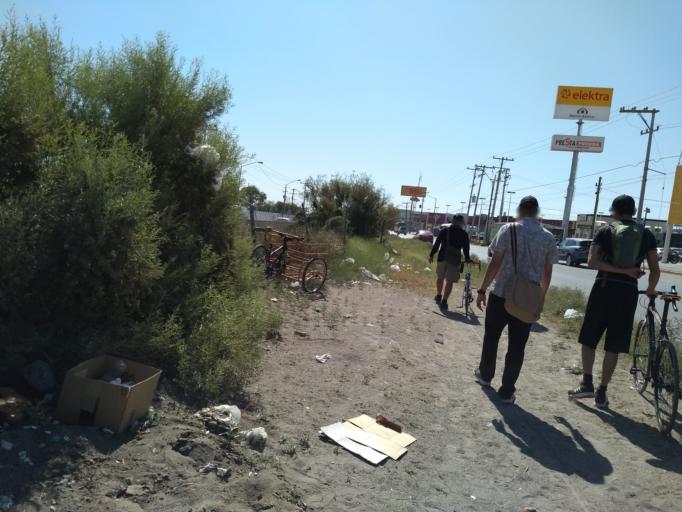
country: US
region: Texas
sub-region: El Paso County
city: El Paso
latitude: 31.7544
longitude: -106.4999
